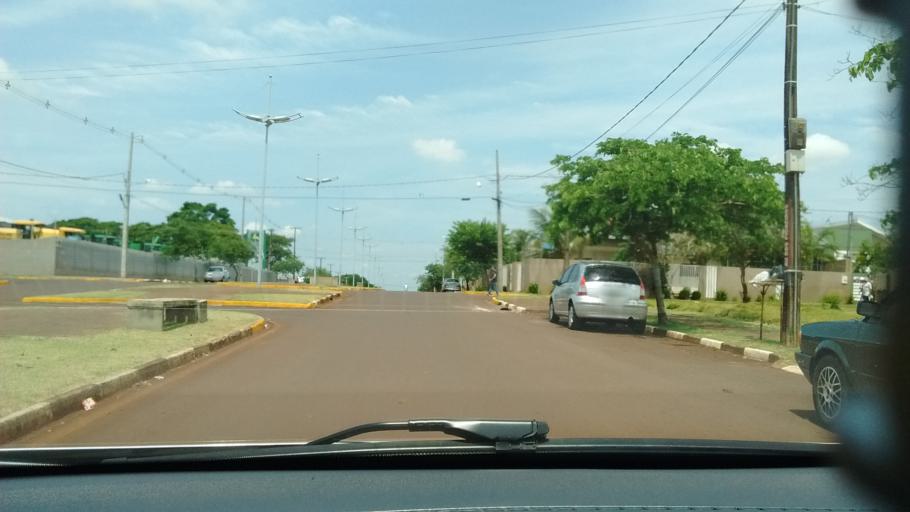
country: BR
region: Parana
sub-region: Corbelia
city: Corbelia
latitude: -24.5502
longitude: -52.9874
